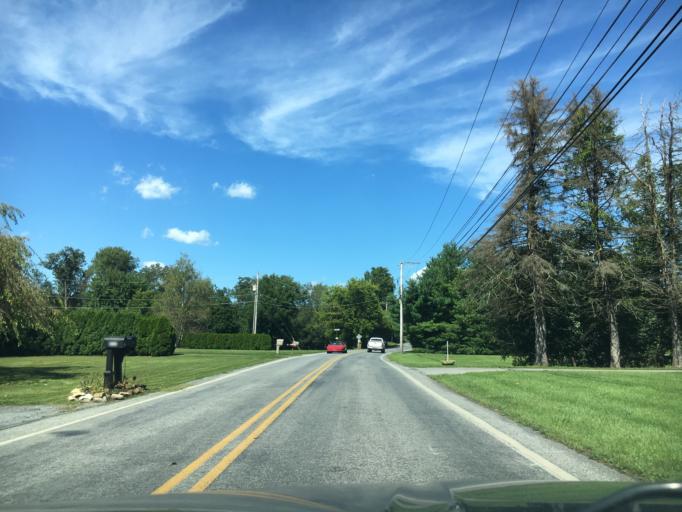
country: US
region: Pennsylvania
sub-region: Berks County
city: Topton
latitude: 40.5192
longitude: -75.6898
